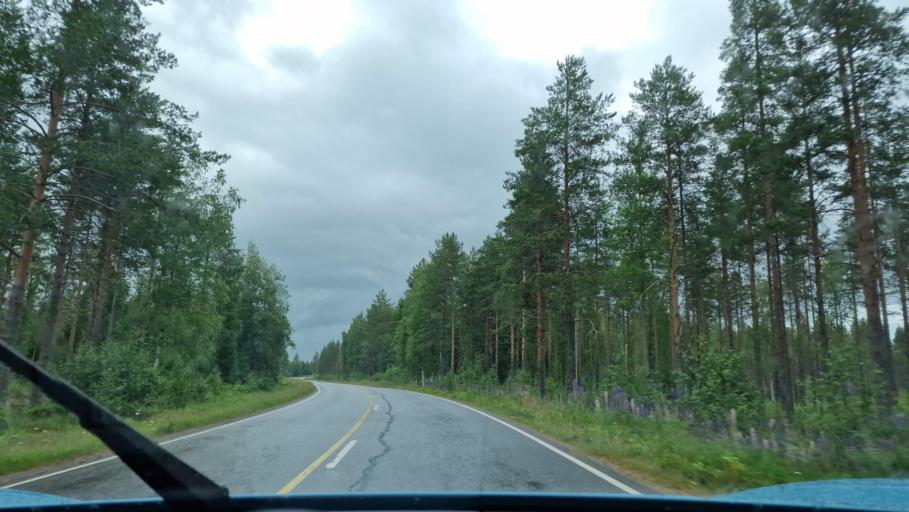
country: FI
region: Southern Ostrobothnia
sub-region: Jaerviseutu
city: Soini
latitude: 62.7771
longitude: 24.3890
